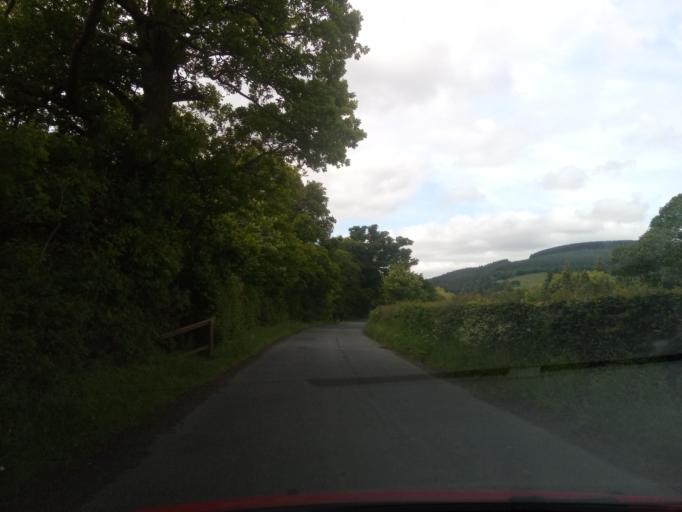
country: GB
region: Scotland
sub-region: The Scottish Borders
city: Selkirk
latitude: 55.5833
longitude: -2.8562
